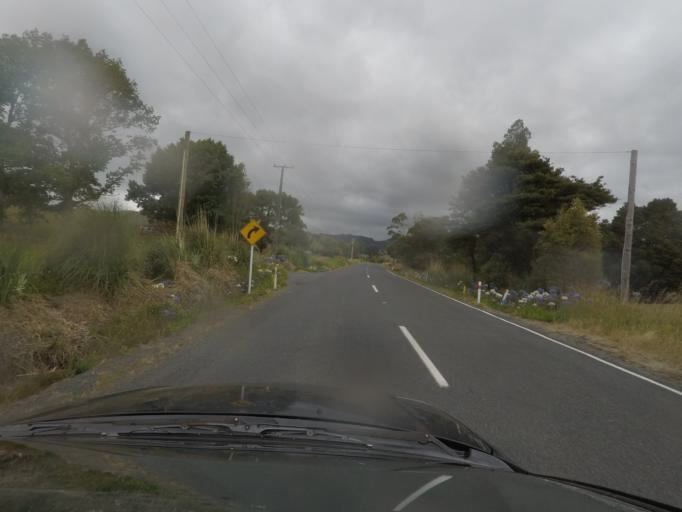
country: NZ
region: Auckland
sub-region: Auckland
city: Warkworth
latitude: -36.2801
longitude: 174.6703
